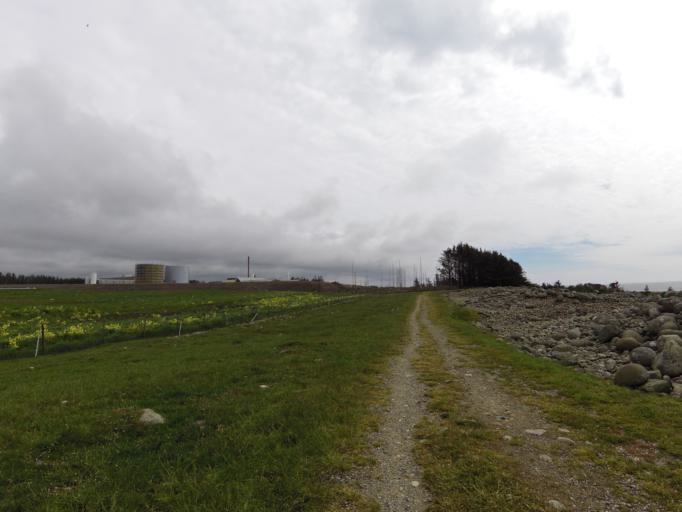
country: NO
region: Rogaland
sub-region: Ha
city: Naerbo
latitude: 58.6325
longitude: 5.5927
